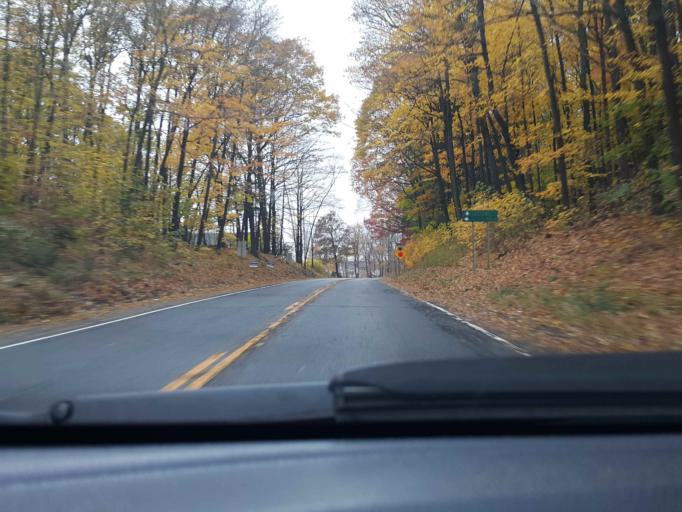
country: US
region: Connecticut
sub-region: Middlesex County
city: Durham
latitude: 41.4612
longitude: -72.6798
